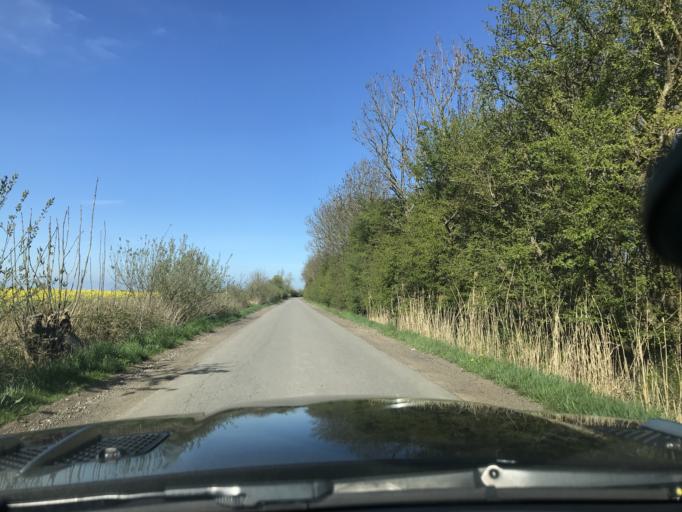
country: DE
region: Schleswig-Holstein
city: Grossenbrode
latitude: 54.4565
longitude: 11.0840
